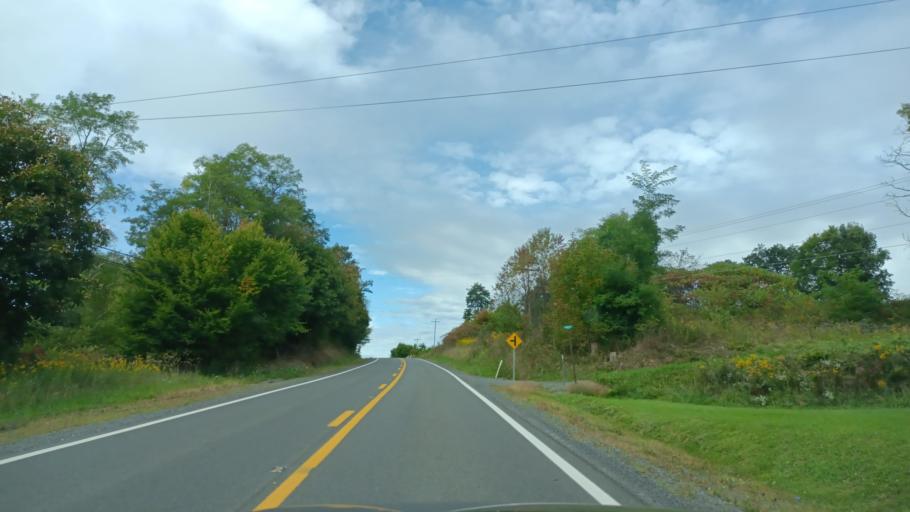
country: US
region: Maryland
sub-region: Garrett County
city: Mountain Lake Park
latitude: 39.2726
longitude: -79.2709
